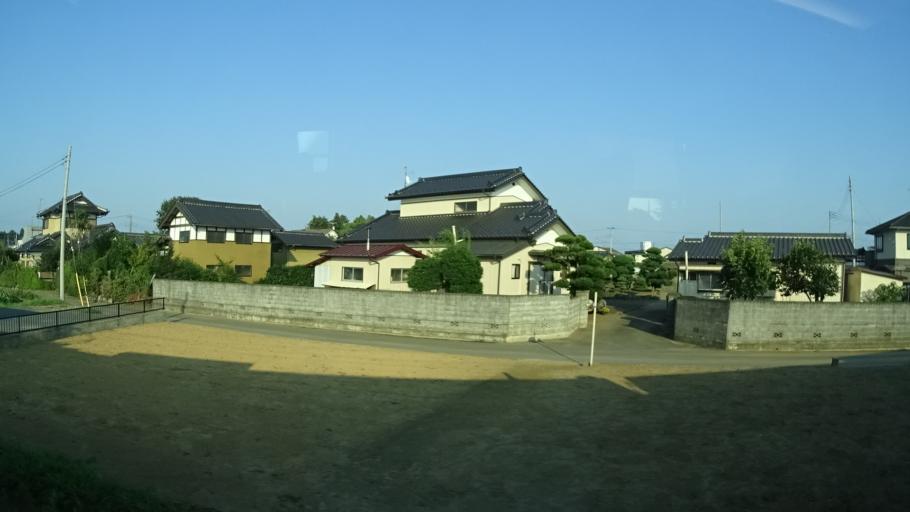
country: JP
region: Ibaraki
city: Hitachi-Naka
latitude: 36.4107
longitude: 140.5310
